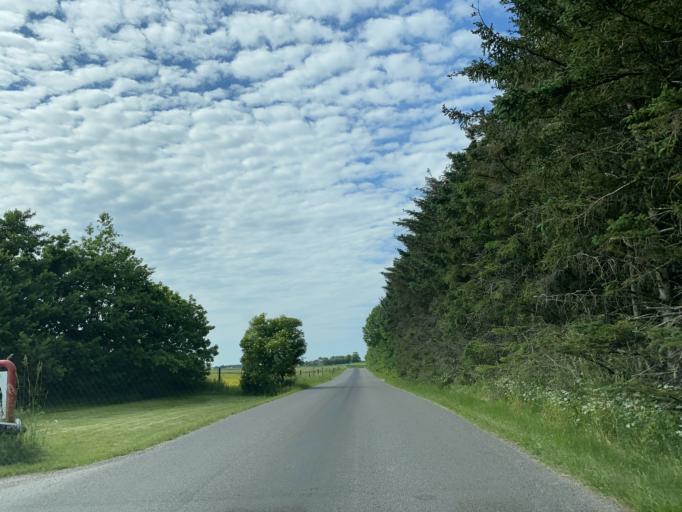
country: DK
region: Central Jutland
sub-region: Skanderborg Kommune
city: Galten
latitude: 56.2117
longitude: 9.8999
